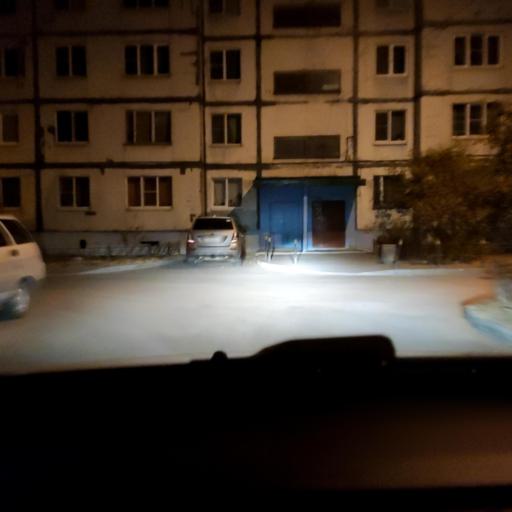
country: RU
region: Voronezj
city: Voronezh
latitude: 51.6364
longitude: 39.2324
